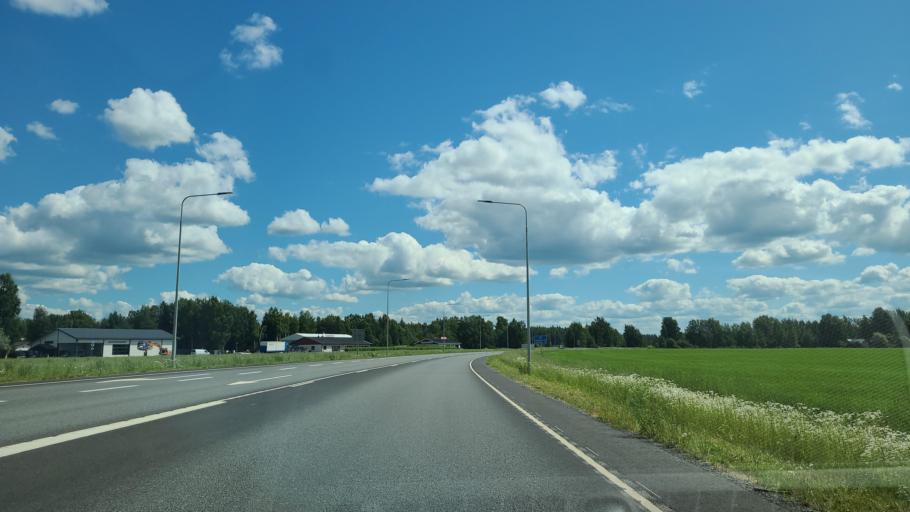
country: FI
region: Southern Ostrobothnia
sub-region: Seinaejoki
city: Ylistaro
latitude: 62.9343
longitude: 22.5085
